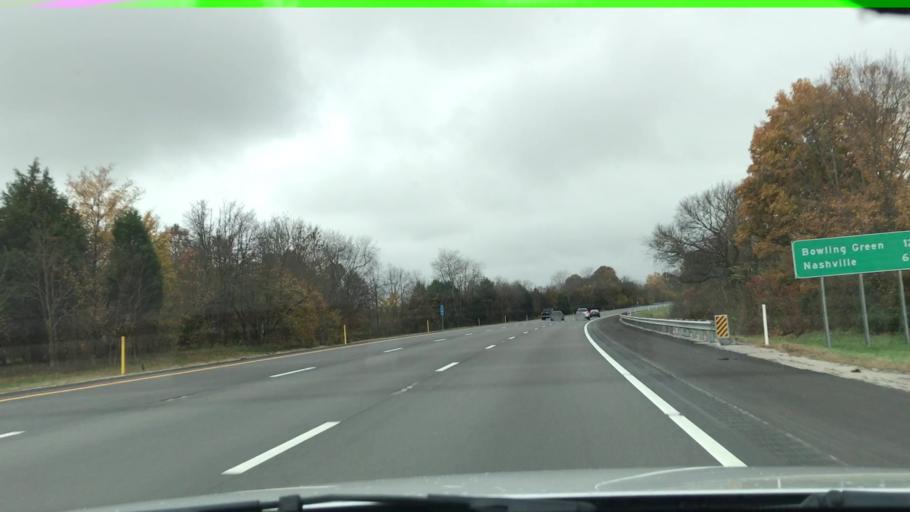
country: US
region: Kentucky
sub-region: Edmonson County
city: Brownsville
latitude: 37.0216
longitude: -86.2514
